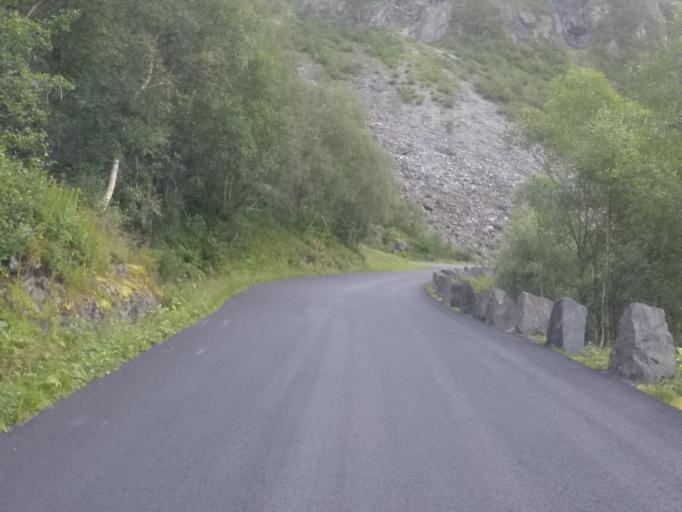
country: NO
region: More og Romsdal
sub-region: Norddal
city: Valldal
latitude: 61.9374
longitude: 7.2663
